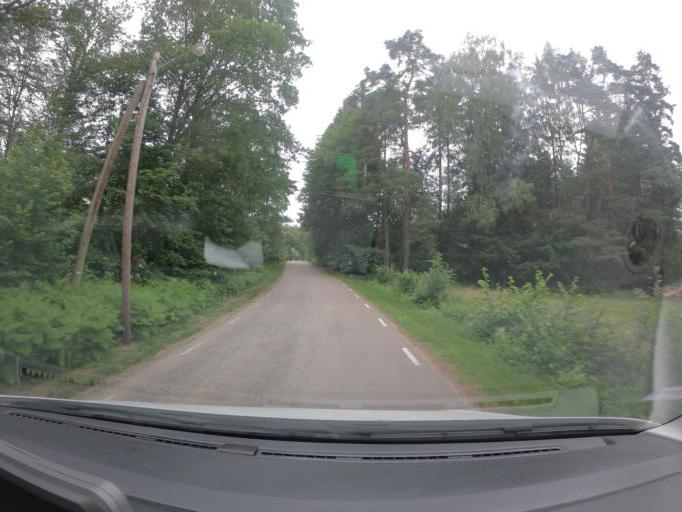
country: SE
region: Skane
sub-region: Klippans Kommun
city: Ljungbyhed
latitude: 56.0367
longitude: 13.2653
